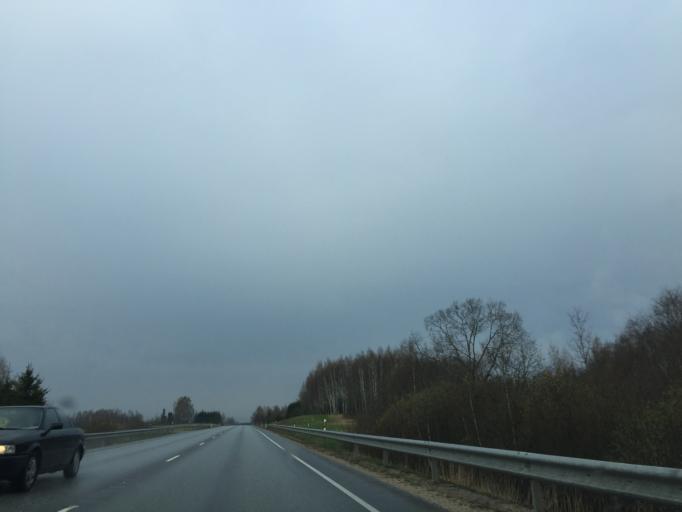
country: EE
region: Tartu
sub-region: UElenurme vald
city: Ulenurme
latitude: 58.1804
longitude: 26.6924
